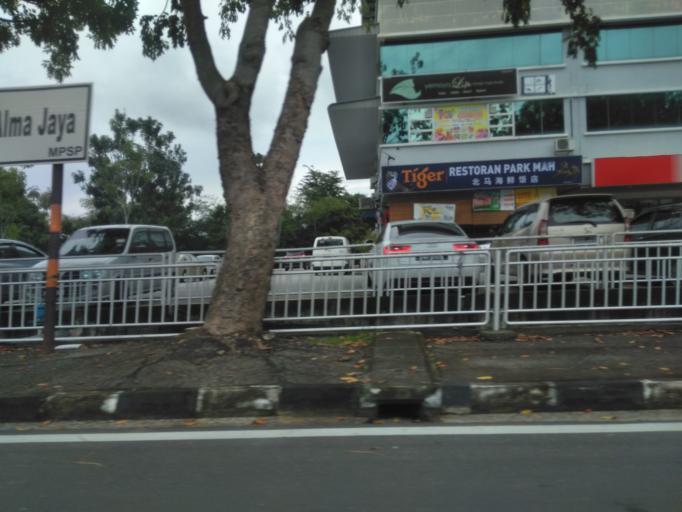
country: MY
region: Penang
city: Bukit Mertajam
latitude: 5.3371
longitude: 100.4836
